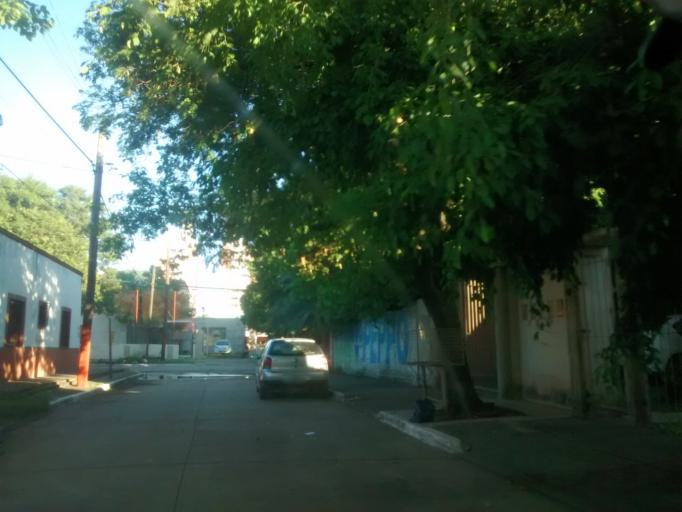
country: AR
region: Chaco
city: Resistencia
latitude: -27.4613
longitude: -58.9760
